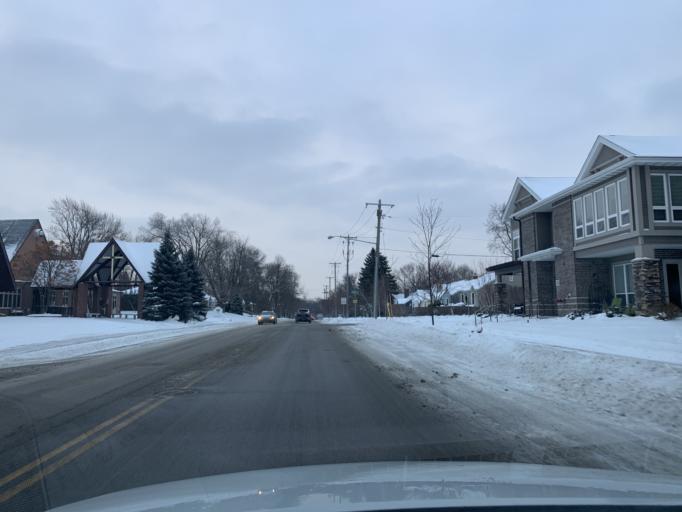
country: US
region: Minnesota
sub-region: Hennepin County
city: Saint Louis Park
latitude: 44.9293
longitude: -93.3469
